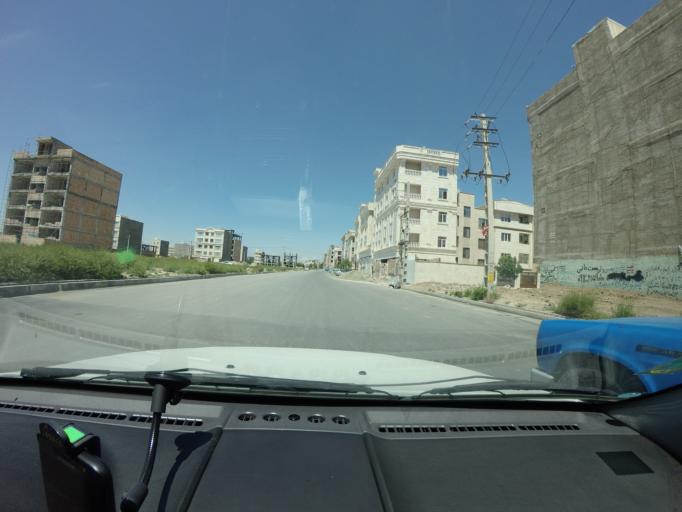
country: IR
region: Tehran
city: Eslamshahr
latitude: 35.5308
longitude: 51.2124
